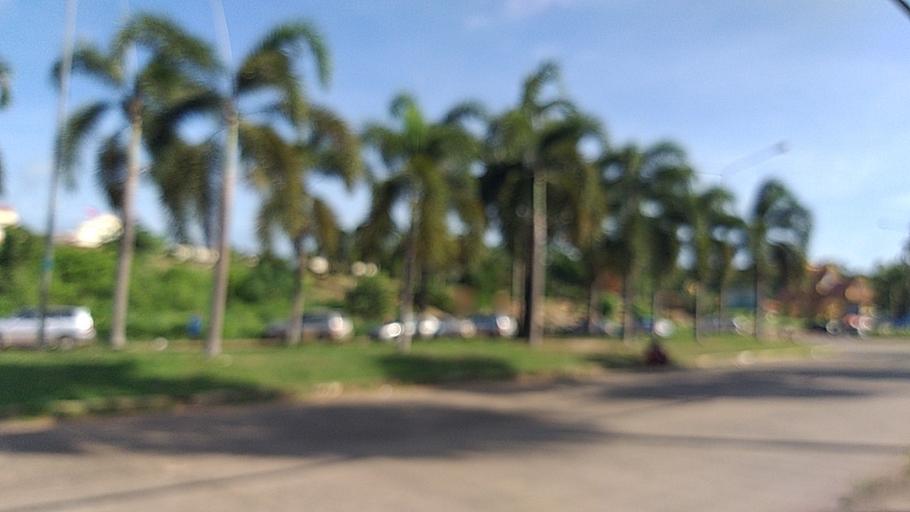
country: TH
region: Surin
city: Kap Choeng
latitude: 14.4329
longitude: 103.6994
